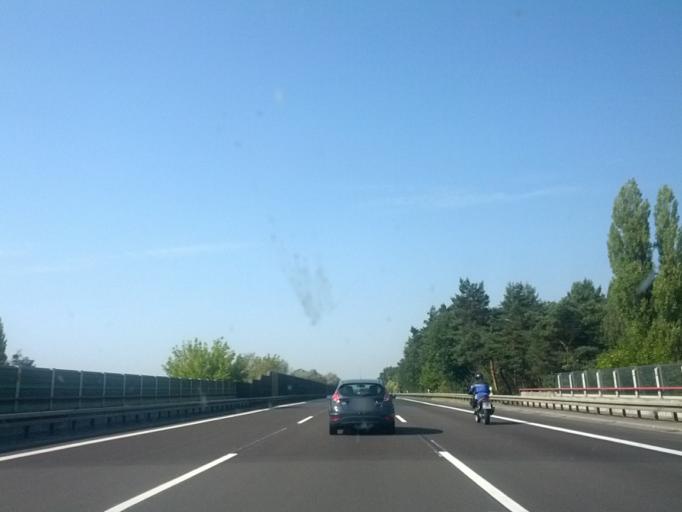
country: DE
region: Brandenburg
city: Ludwigsfelde
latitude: 52.3069
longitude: 13.2702
